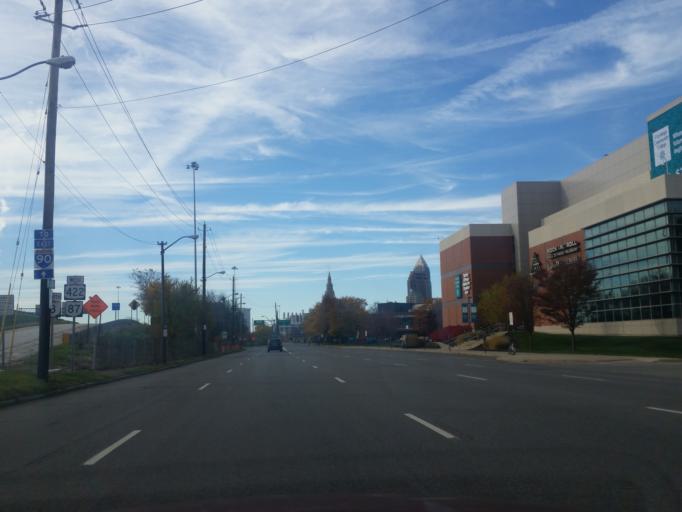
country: US
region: Ohio
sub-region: Cuyahoga County
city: Cleveland
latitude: 41.4915
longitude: -81.6689
